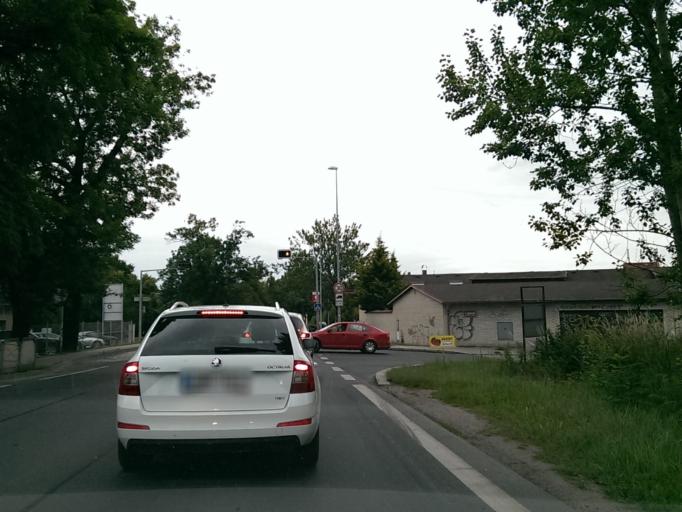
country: CZ
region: Praha
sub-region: Praha 14
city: Dolni Pocernice
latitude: 50.0549
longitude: 14.5638
